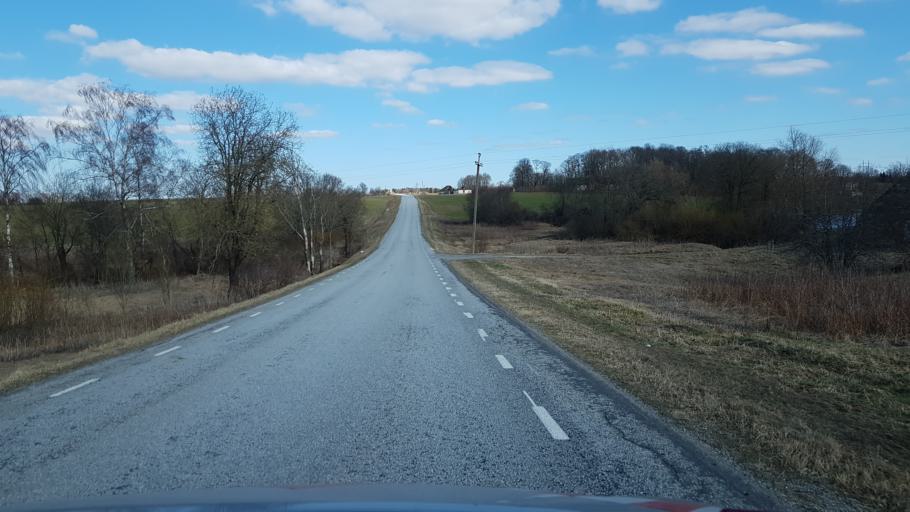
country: EE
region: Laeaene-Virumaa
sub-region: Kadrina vald
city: Kadrina
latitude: 59.2898
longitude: 26.1805
